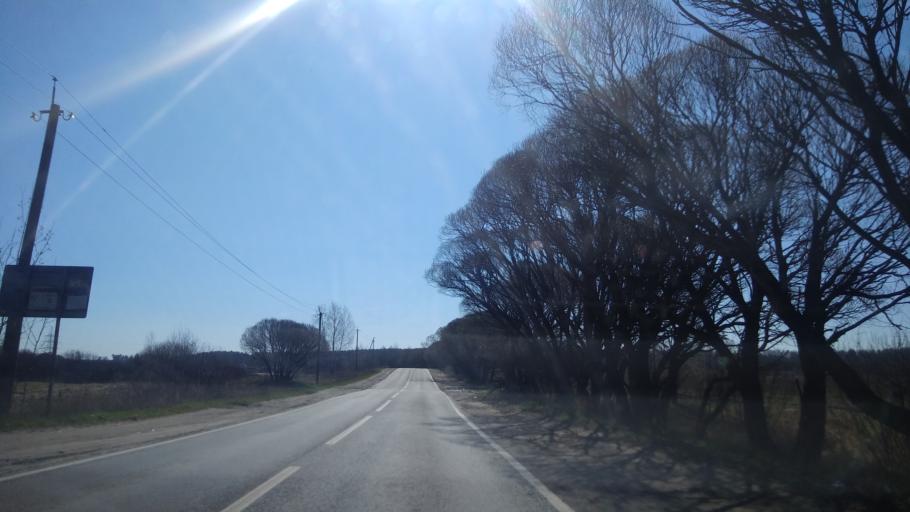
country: RU
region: Moskovskaya
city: Pravdinskiy
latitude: 56.0459
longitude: 37.8816
